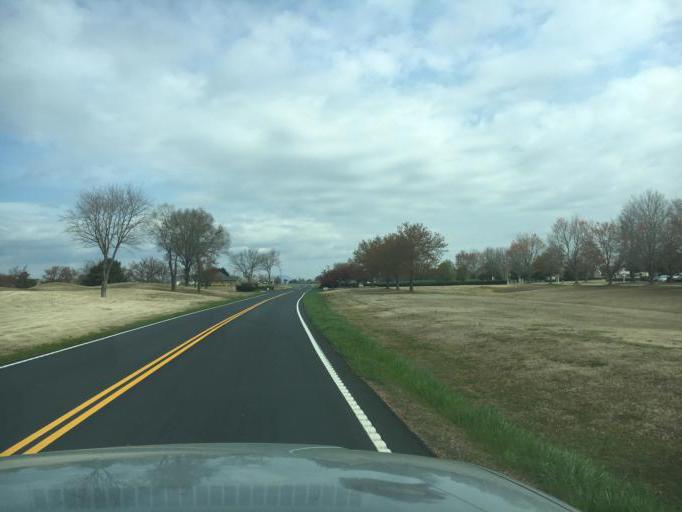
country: US
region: South Carolina
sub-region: Spartanburg County
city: Landrum
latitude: 35.1096
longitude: -82.2131
